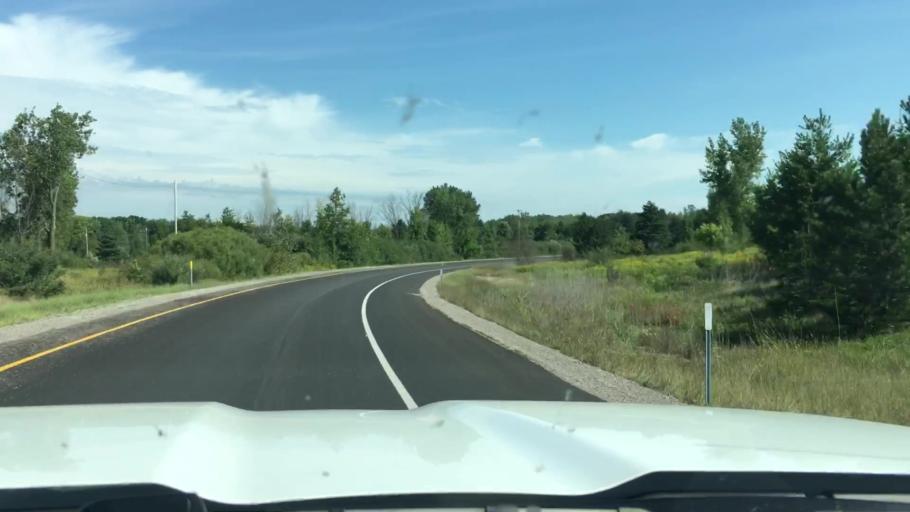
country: US
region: Michigan
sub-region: Bay County
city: Auburn
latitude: 43.5955
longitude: -84.1388
